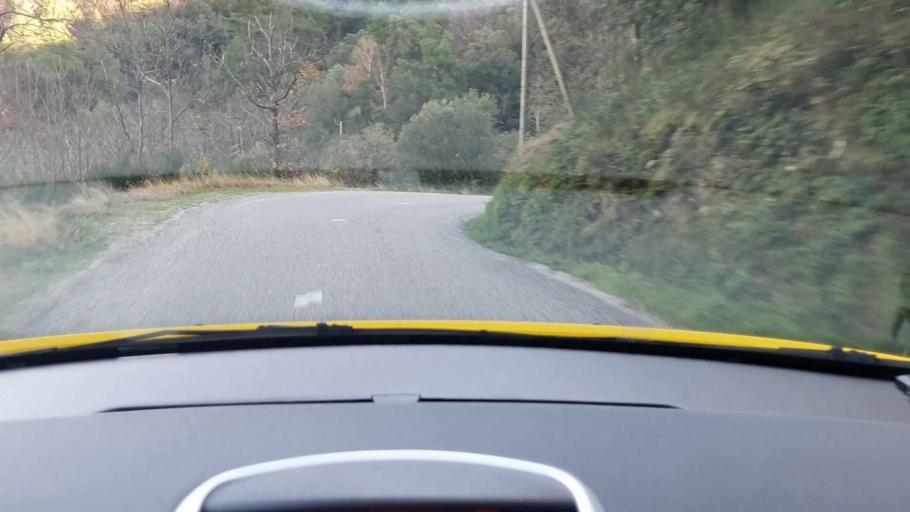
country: FR
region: Languedoc-Roussillon
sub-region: Departement du Gard
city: Branoux-les-Taillades
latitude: 44.2800
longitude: 3.9833
